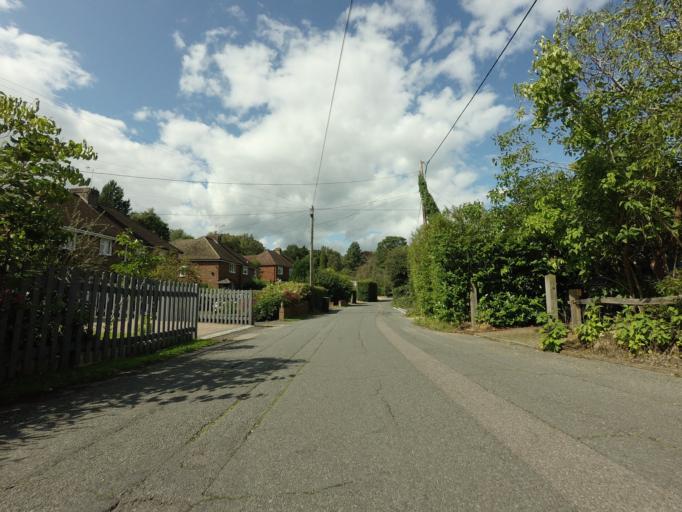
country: GB
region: England
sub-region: Kent
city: Borough Green
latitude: 51.2785
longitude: 0.2744
